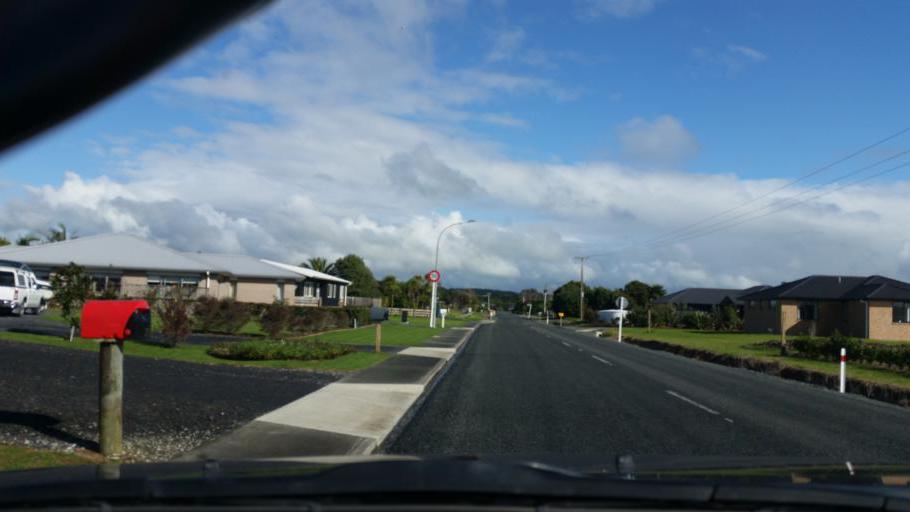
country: NZ
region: Auckland
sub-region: Auckland
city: Wellsford
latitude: -36.0879
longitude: 174.5753
